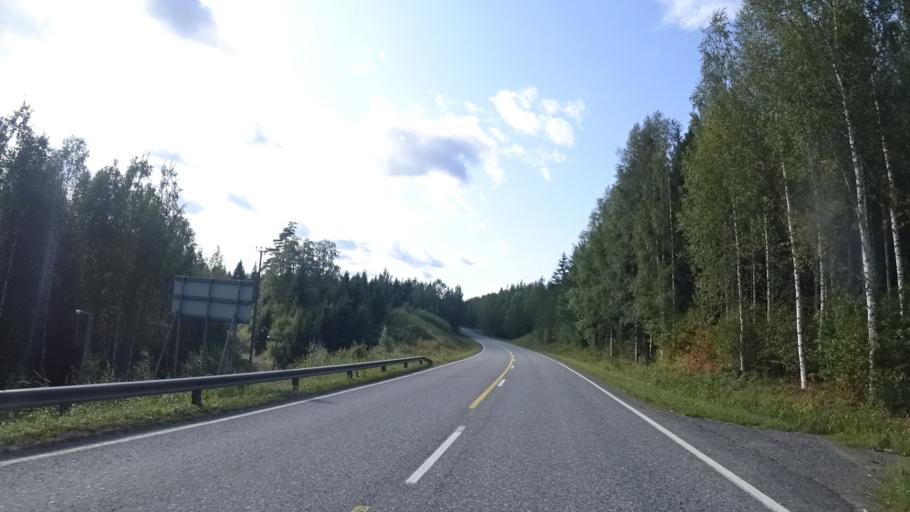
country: FI
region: North Karelia
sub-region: Keski-Karjala
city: Kitee
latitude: 62.0880
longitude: 30.1349
